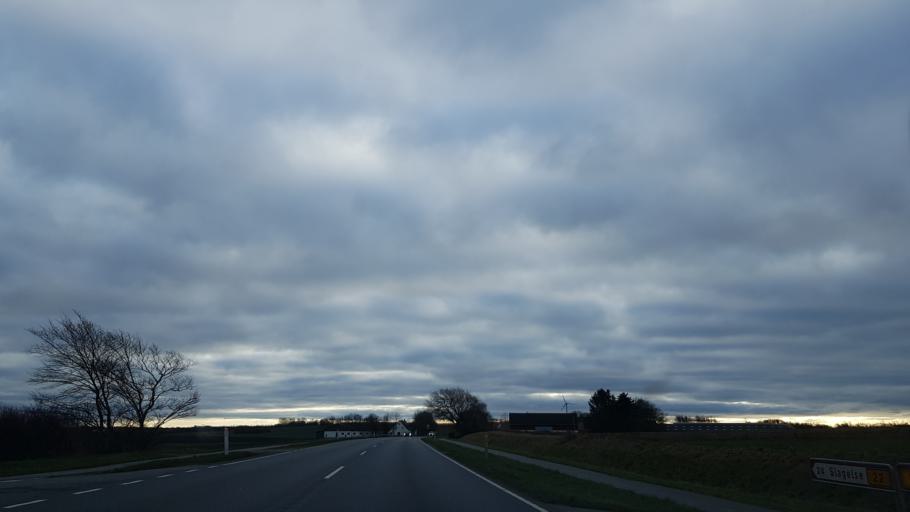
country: DK
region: Zealand
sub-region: Kalundborg Kommune
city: Gorlev
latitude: 55.5800
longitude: 11.1900
